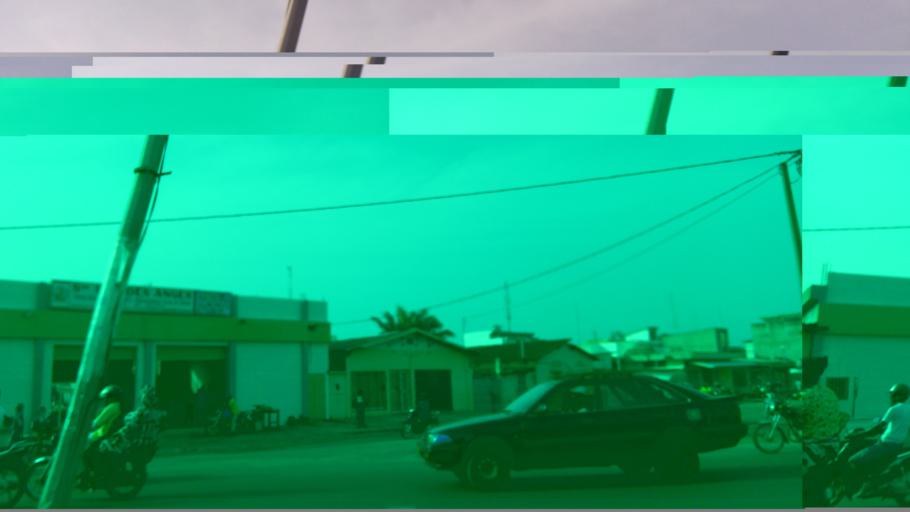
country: BJ
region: Littoral
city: Cotonou
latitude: 6.3703
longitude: 2.4241
